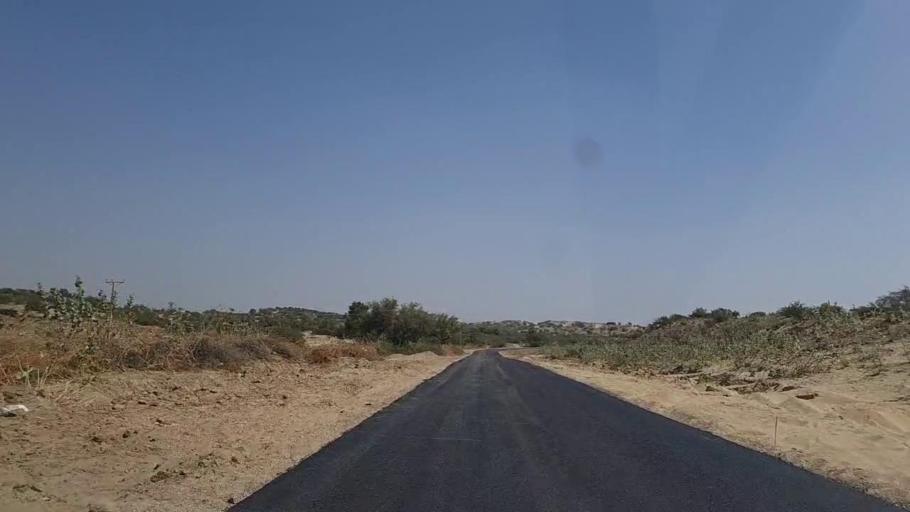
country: PK
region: Sindh
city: Diplo
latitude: 24.4808
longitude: 69.5211
